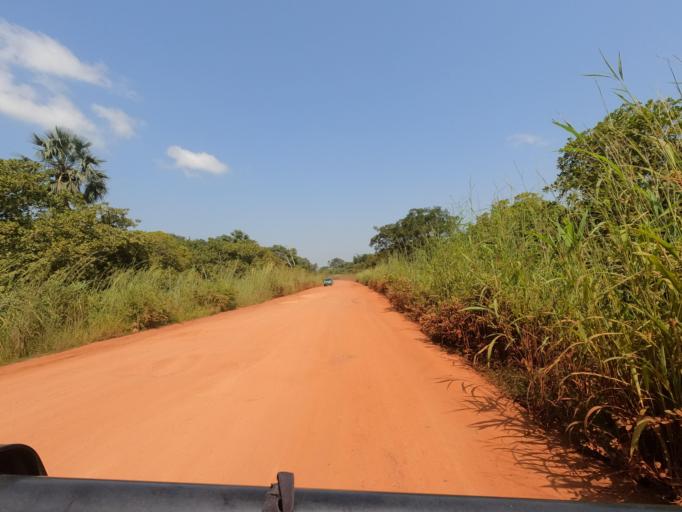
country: GW
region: Oio
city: Bissora
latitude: 12.3489
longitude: -15.7640
